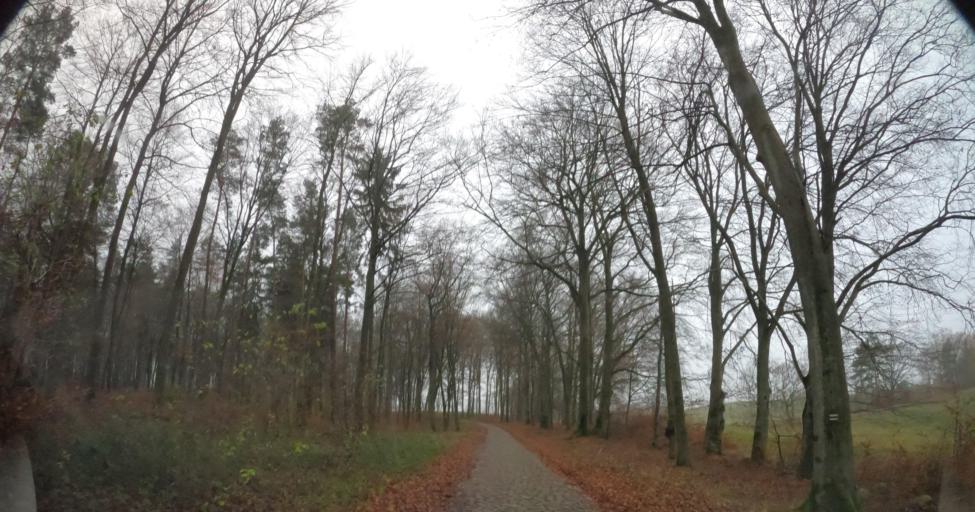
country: PL
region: West Pomeranian Voivodeship
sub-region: Powiat drawski
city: Drawsko Pomorskie
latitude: 53.5567
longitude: 15.7237
